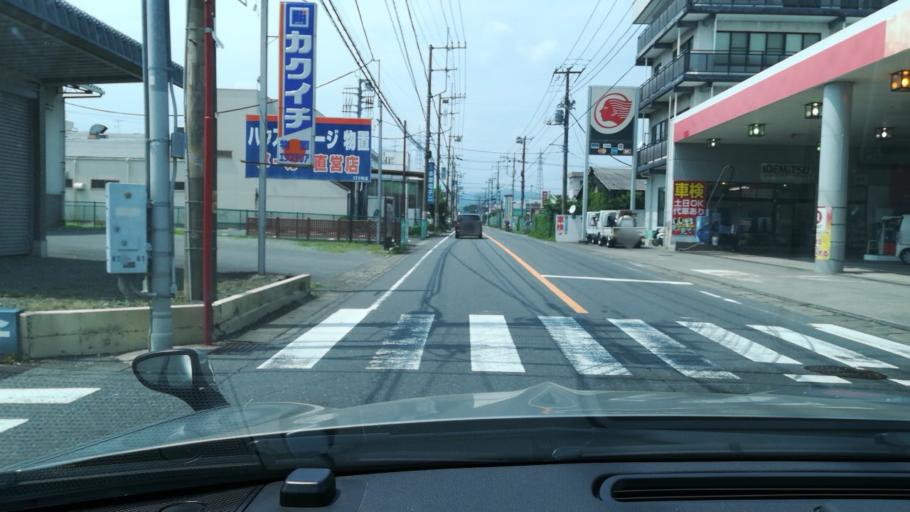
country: JP
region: Tokyo
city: Hachioji
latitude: 35.5895
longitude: 139.3330
